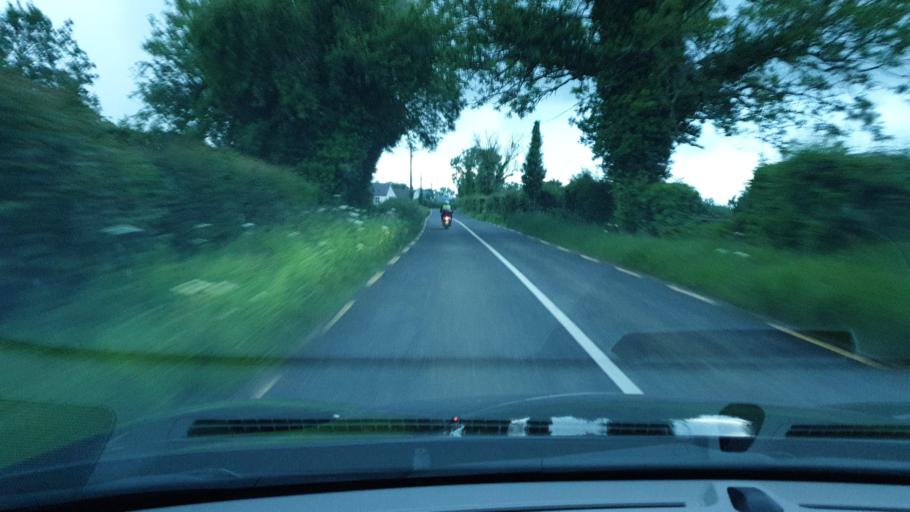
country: IE
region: Leinster
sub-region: An Mhi
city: Ashbourne
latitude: 53.5101
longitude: -6.3195
